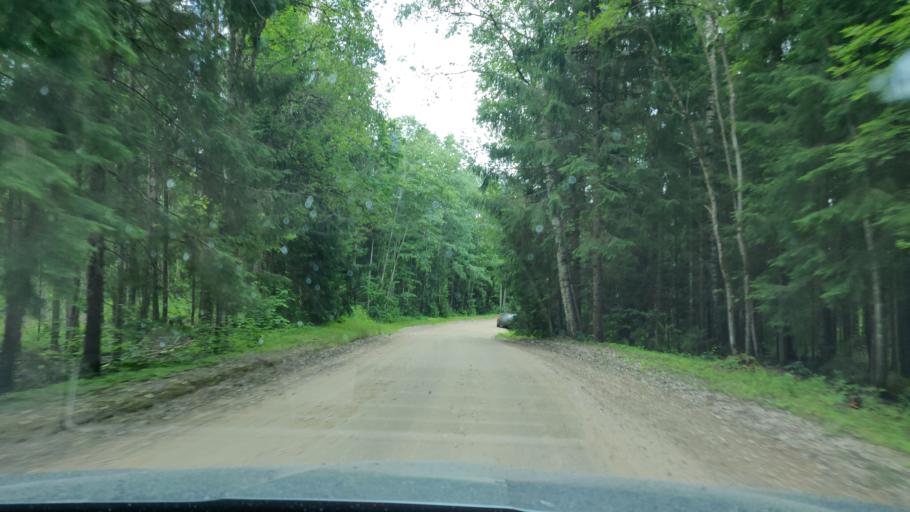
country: EE
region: Vorumaa
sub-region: Antsla vald
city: Vana-Antsla
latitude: 58.0307
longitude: 26.5498
